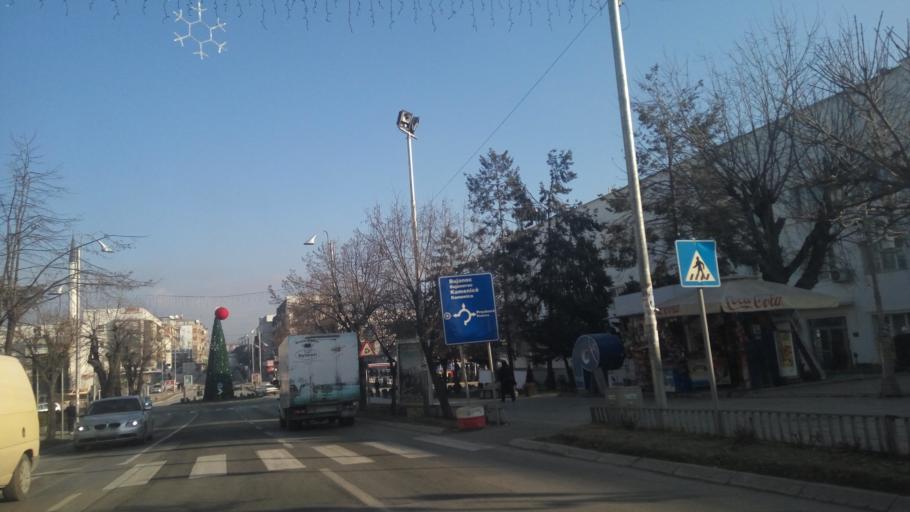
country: XK
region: Gjilan
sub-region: Komuna e Gjilanit
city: Gjilan
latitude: 42.4628
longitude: 21.4689
